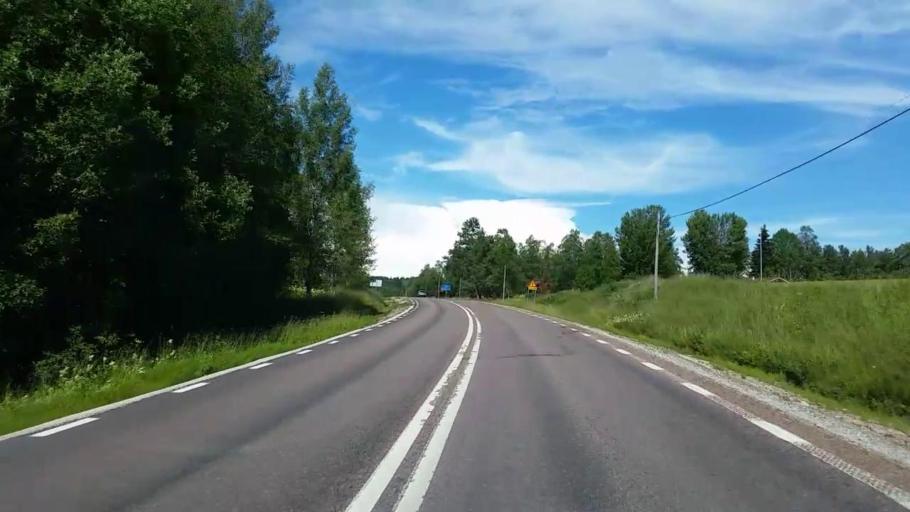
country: SE
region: Dalarna
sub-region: Rattviks Kommun
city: Raettvik
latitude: 61.0063
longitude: 15.2196
